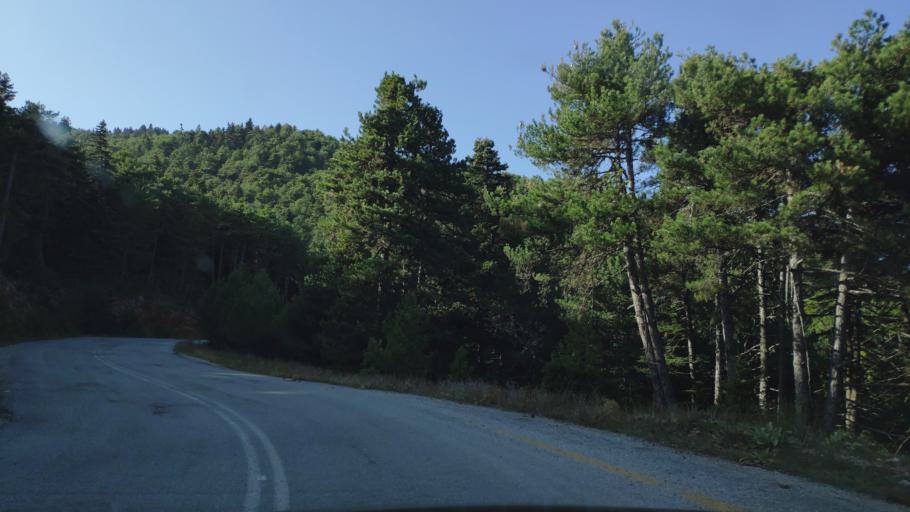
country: GR
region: West Greece
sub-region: Nomos Achaias
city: Aiyira
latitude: 38.0188
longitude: 22.4045
